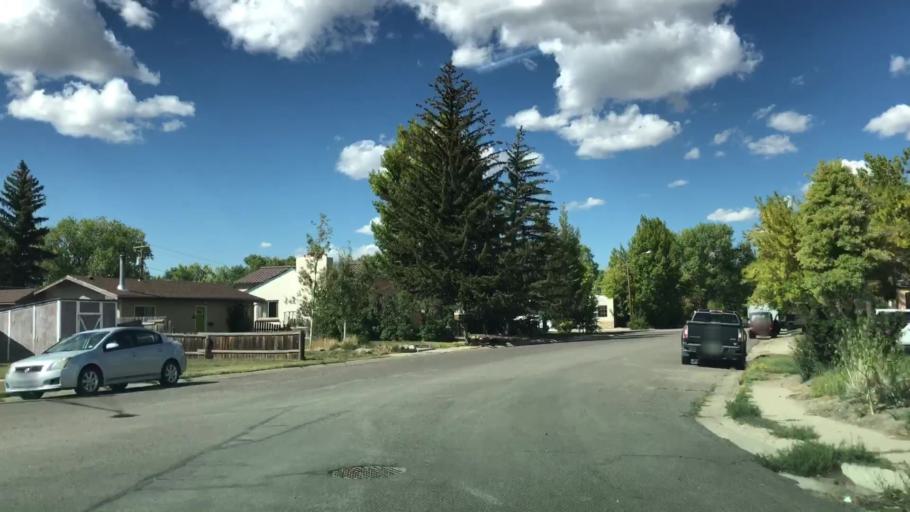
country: US
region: Wyoming
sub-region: Albany County
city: Laramie
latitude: 41.3014
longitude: -105.5919
